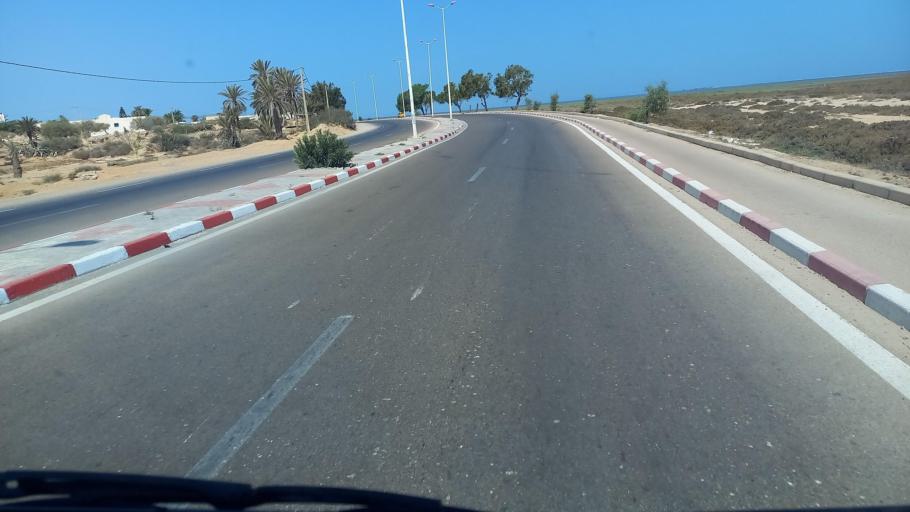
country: TN
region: Madanin
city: Houmt Souk
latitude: 33.8715
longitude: 10.9357
